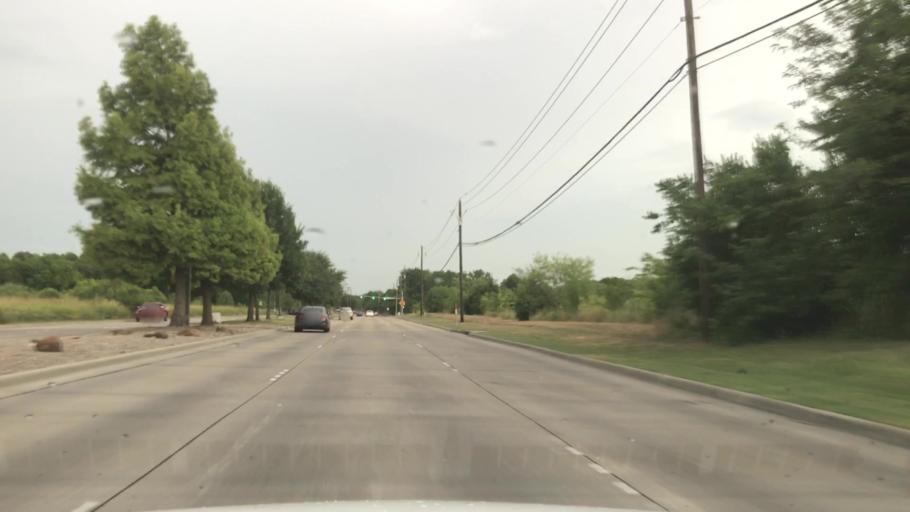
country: US
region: Texas
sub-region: Dallas County
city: Mesquite
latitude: 32.7403
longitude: -96.5749
